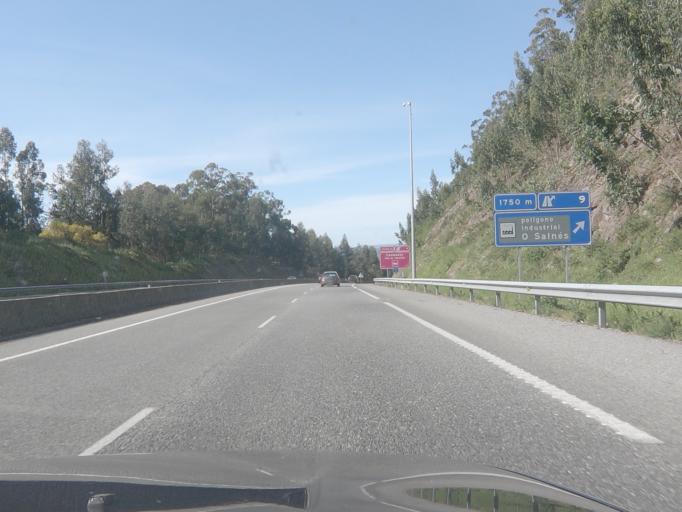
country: ES
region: Galicia
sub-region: Provincia de Pontevedra
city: Meis
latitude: 42.4782
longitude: -8.7709
